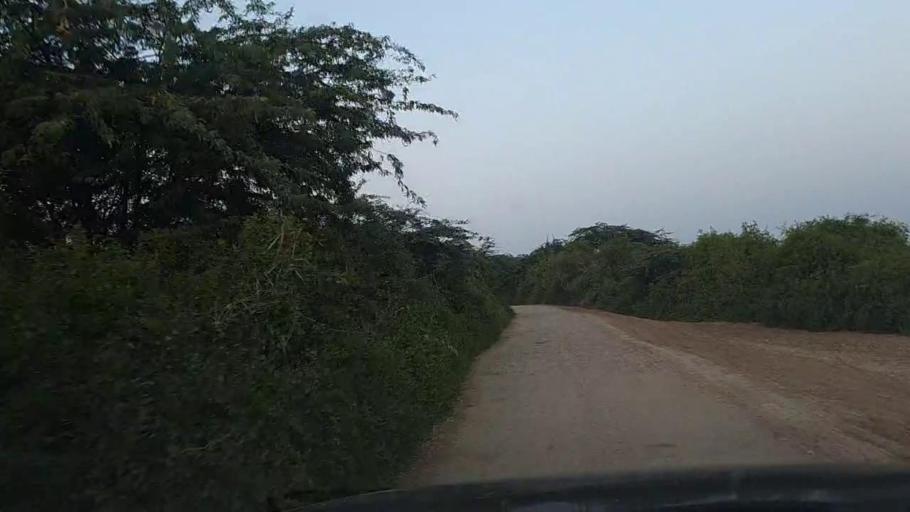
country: PK
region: Sindh
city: Mirpur Sakro
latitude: 24.6312
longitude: 67.6568
